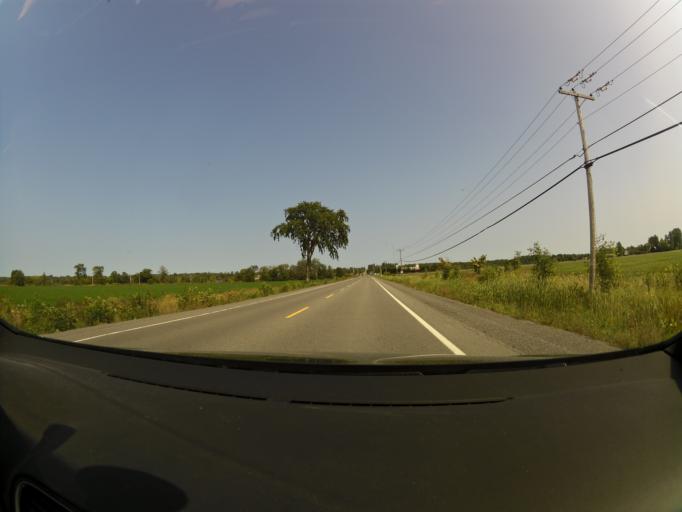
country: CA
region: Ontario
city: Arnprior
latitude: 45.4561
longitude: -76.2040
